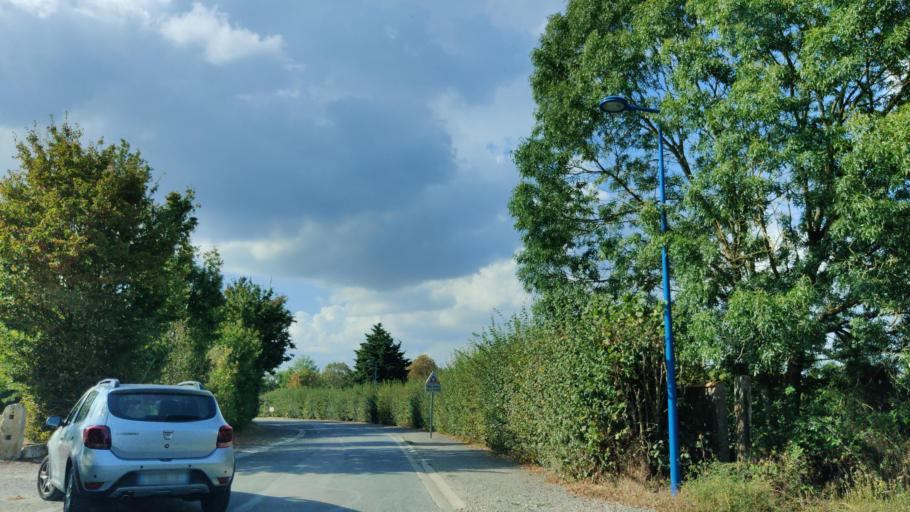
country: FR
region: Poitou-Charentes
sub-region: Departement des Deux-Sevres
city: Bessines
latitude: 46.2995
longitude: -0.5101
